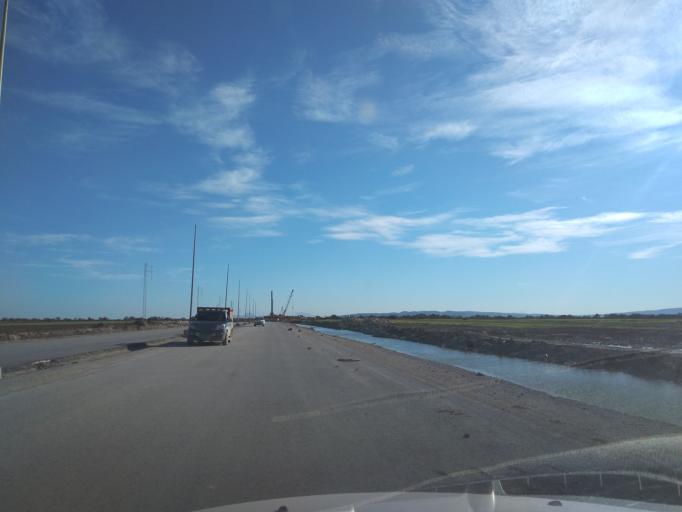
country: TN
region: Ariana
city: Qal'at al Andalus
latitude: 37.0279
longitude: 10.1380
